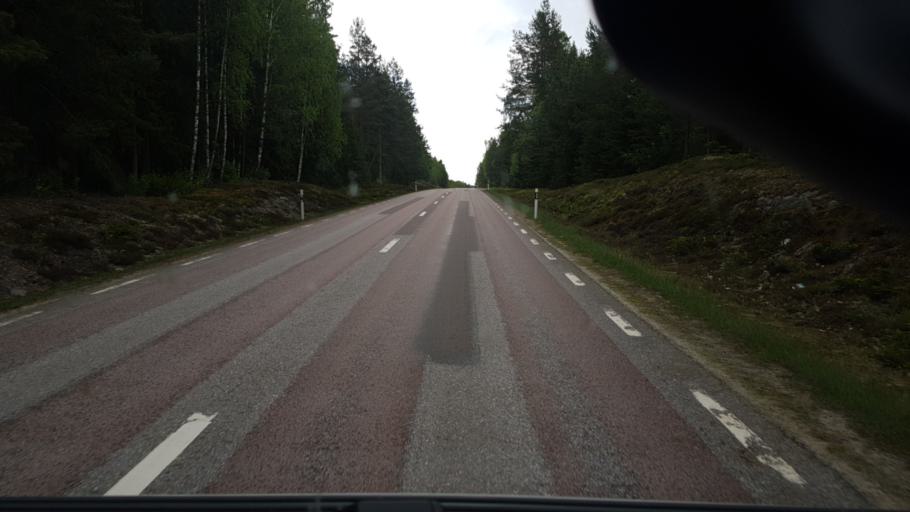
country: SE
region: Vaermland
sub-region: Arvika Kommun
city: Arvika
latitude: 59.5703
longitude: 12.7156
